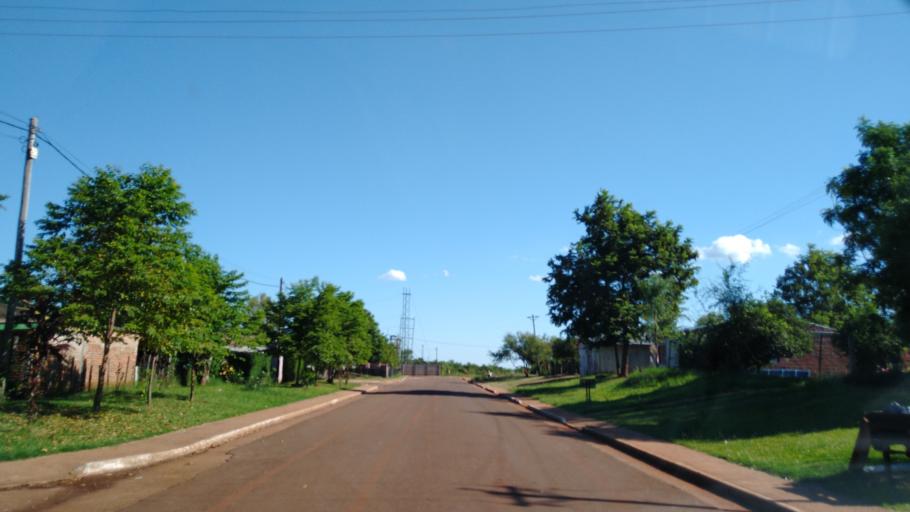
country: AR
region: Misiones
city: Garupa
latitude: -27.4894
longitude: -55.8220
